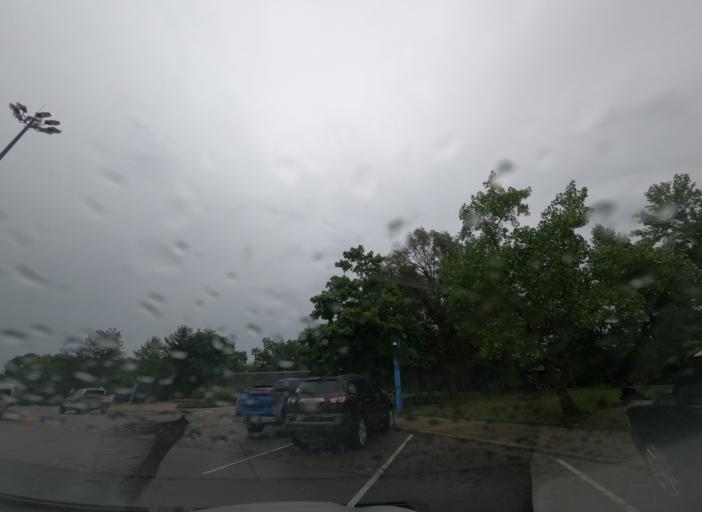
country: US
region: Illinois
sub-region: Madison County
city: Highland
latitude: 38.7850
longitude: -89.7030
